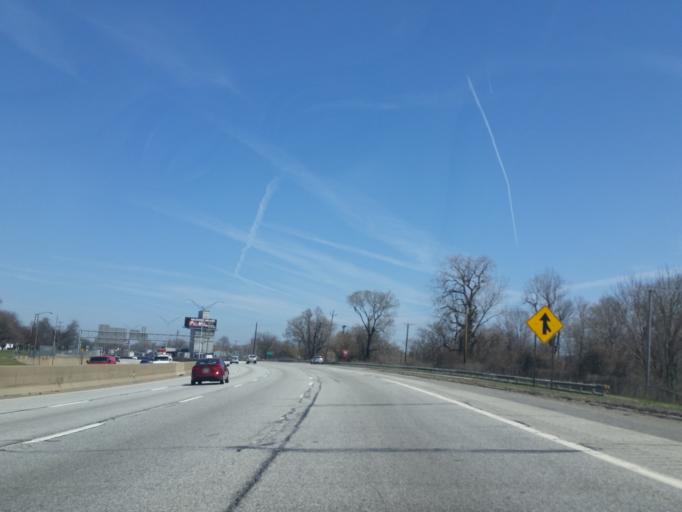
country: US
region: Ohio
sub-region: Cuyahoga County
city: Bratenahl
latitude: 41.5391
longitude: -81.6298
